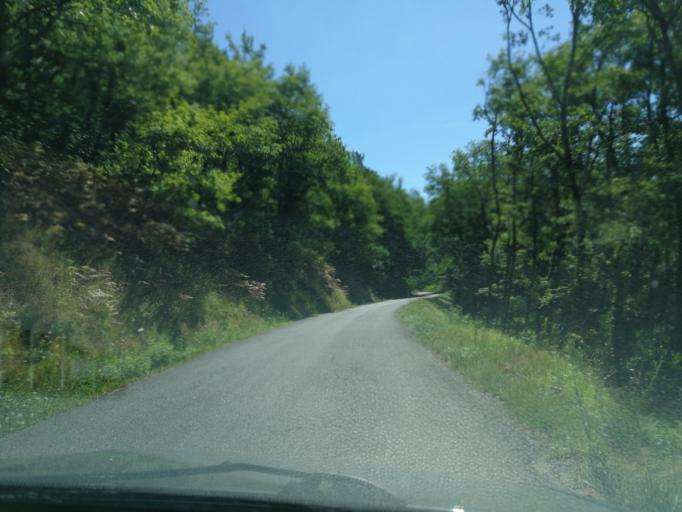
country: FR
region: Limousin
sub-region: Departement de la Correze
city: Argentat
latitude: 45.0921
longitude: 1.9007
